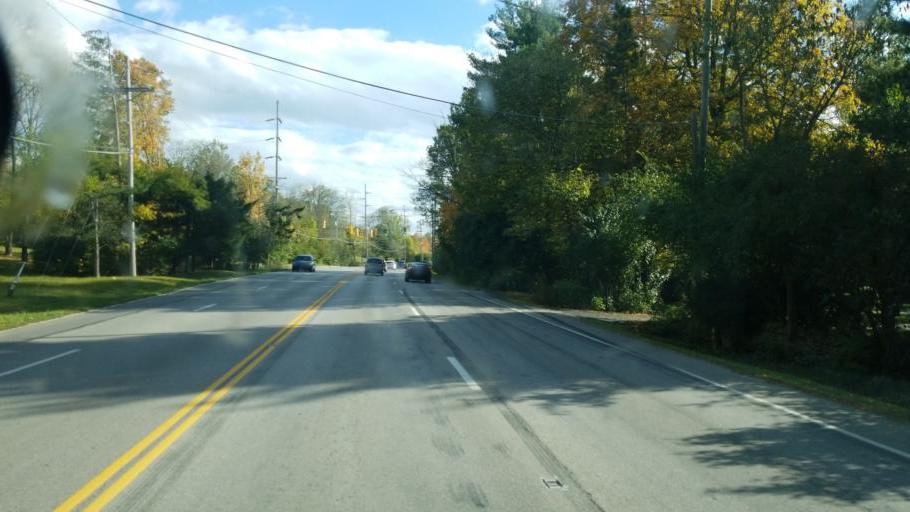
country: US
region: Ohio
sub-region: Franklin County
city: Dublin
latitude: 40.1334
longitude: -83.1137
